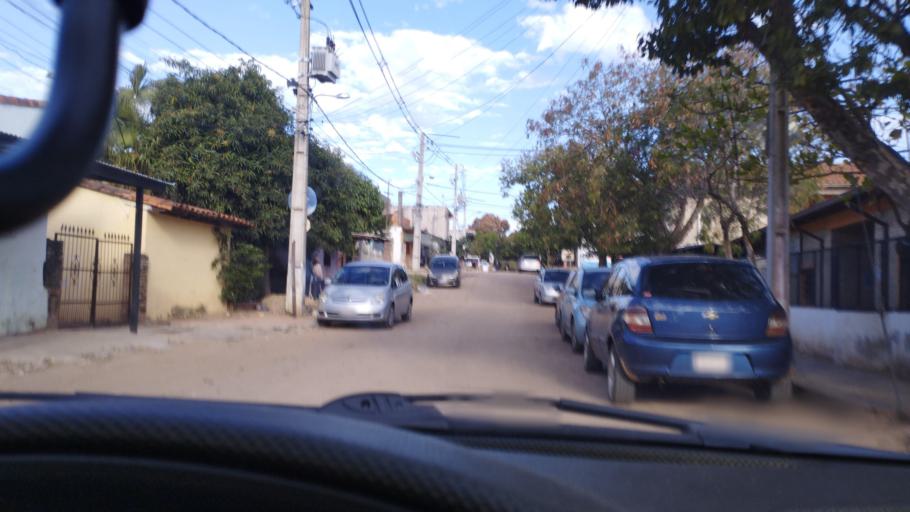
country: PY
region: Central
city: Colonia Mariano Roque Alonso
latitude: -25.2395
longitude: -57.5812
